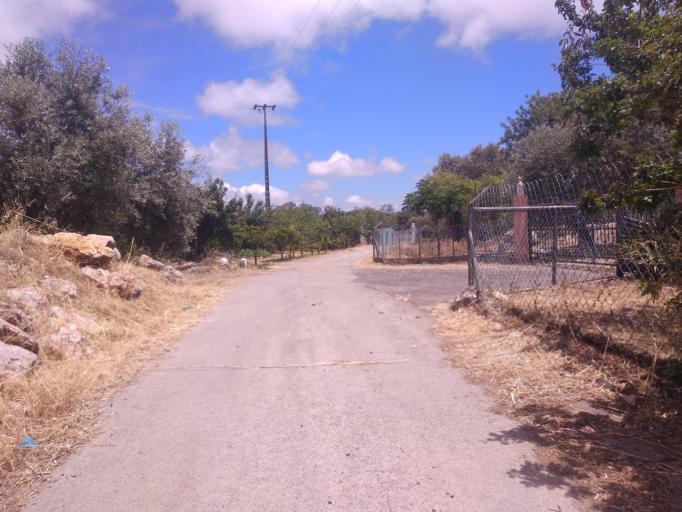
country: PT
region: Faro
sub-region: Sao Bras de Alportel
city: Sao Bras de Alportel
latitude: 37.1655
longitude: -7.9020
